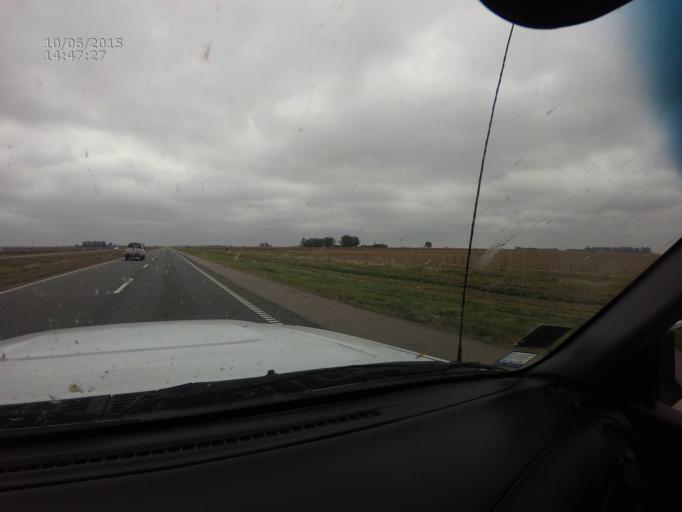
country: AR
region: Cordoba
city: Oliva
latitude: -31.9580
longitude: -63.5919
